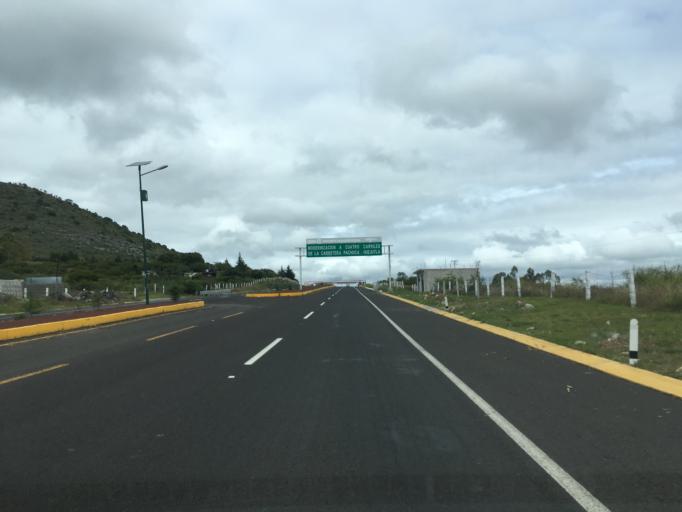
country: MX
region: Hidalgo
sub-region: Atotonilco el Grande
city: La Estancia
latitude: 20.3315
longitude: -98.7017
